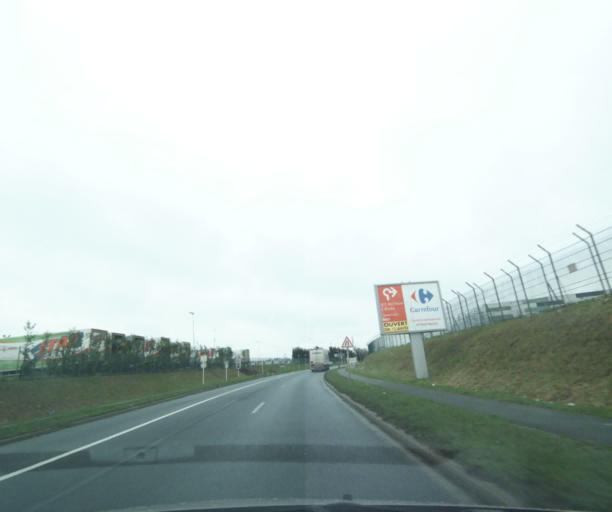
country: FR
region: Ile-de-France
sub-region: Departement du Val-de-Marne
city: Villeneuve-le-Roi
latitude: 48.7269
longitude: 2.4071
